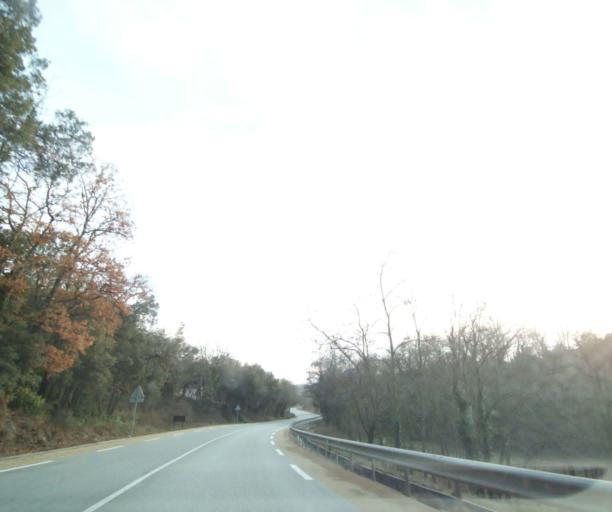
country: FR
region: Provence-Alpes-Cote d'Azur
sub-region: Departement du Var
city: Trans-en-Provence
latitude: 43.4989
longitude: 6.5101
